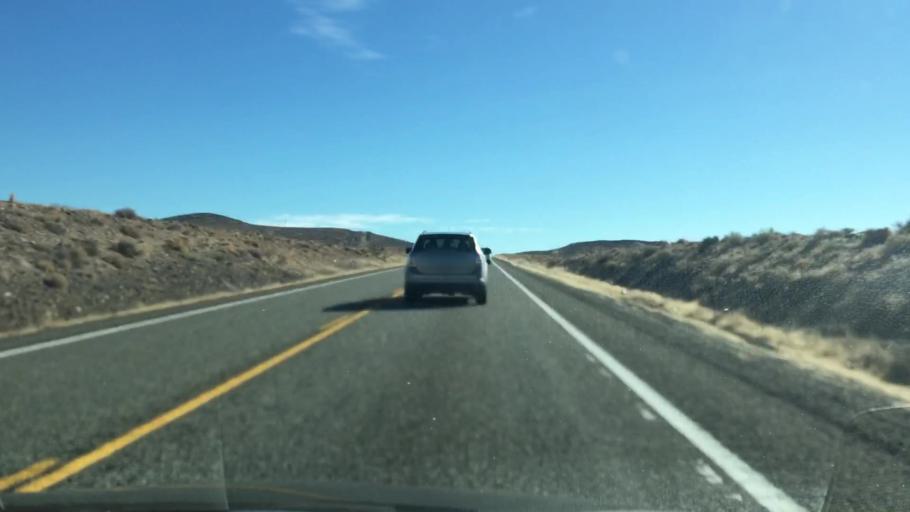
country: US
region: Nevada
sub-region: Lyon County
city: Silver Springs
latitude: 39.2337
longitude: -119.2319
